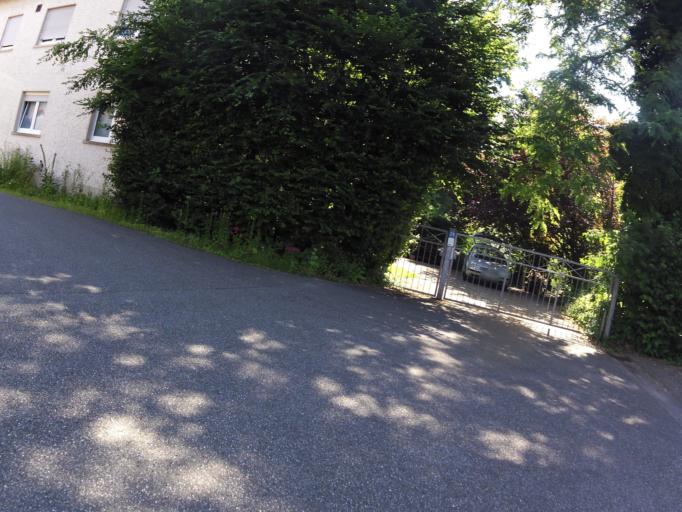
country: DE
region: Baden-Wuerttemberg
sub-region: Freiburg Region
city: Hohberg
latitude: 48.3383
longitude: 7.8966
